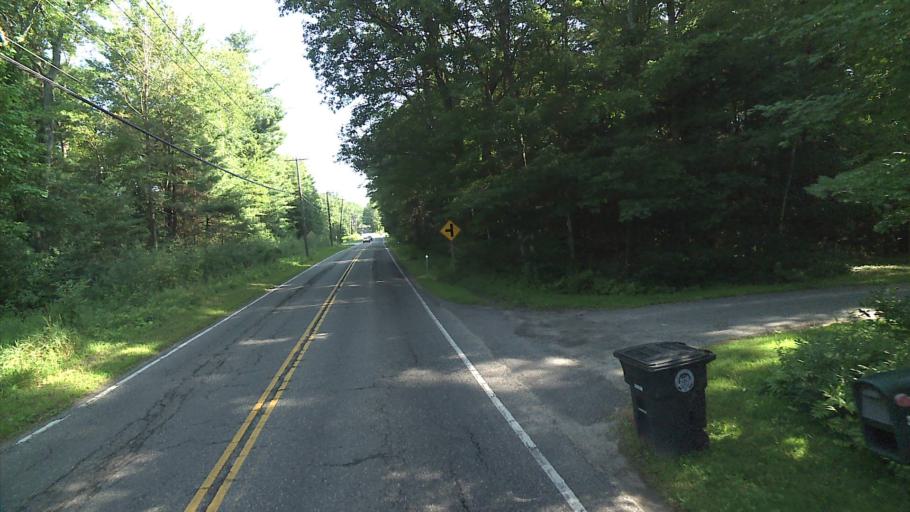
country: US
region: Connecticut
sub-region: Litchfield County
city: Winsted
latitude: 41.8741
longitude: -73.0674
